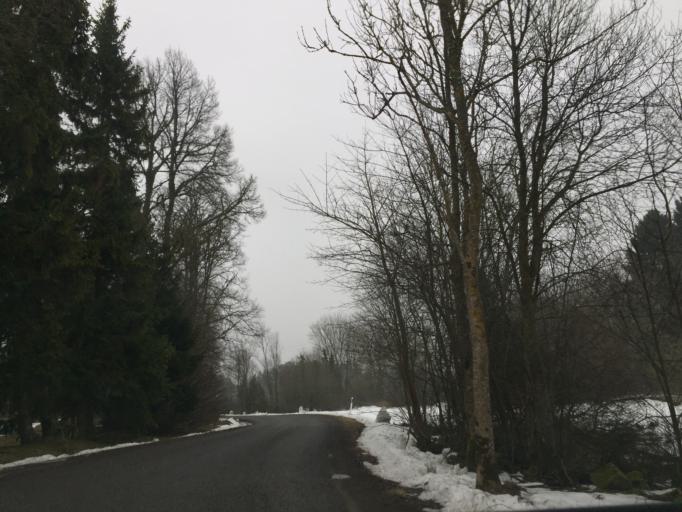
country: EE
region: Saare
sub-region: Kuressaare linn
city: Kuressaare
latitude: 58.2712
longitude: 22.5828
